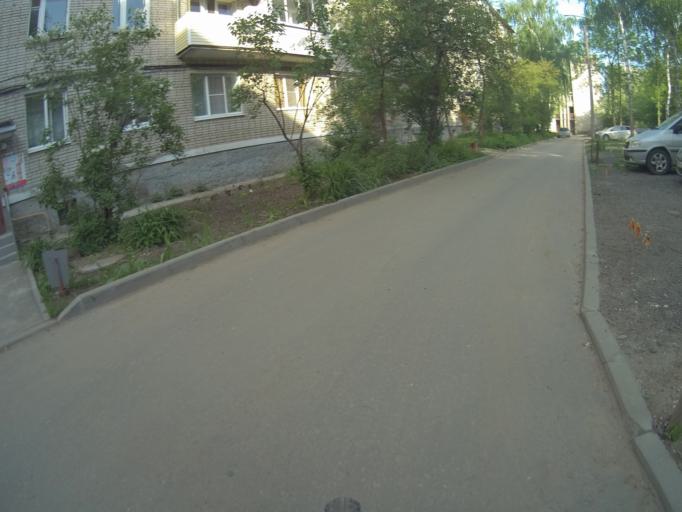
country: RU
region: Vladimir
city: Bogolyubovo
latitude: 56.1683
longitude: 40.4771
